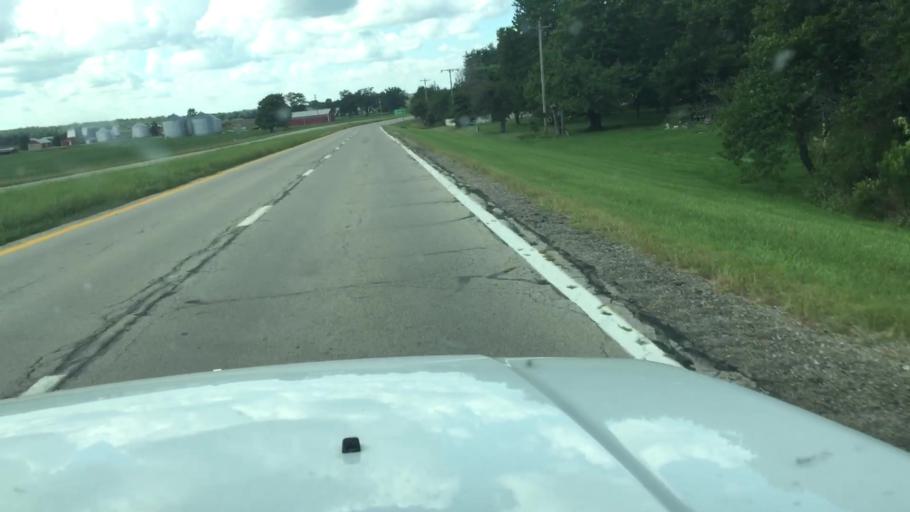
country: US
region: Ohio
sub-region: Madison County
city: Choctaw Lake
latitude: 39.9329
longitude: -83.4932
